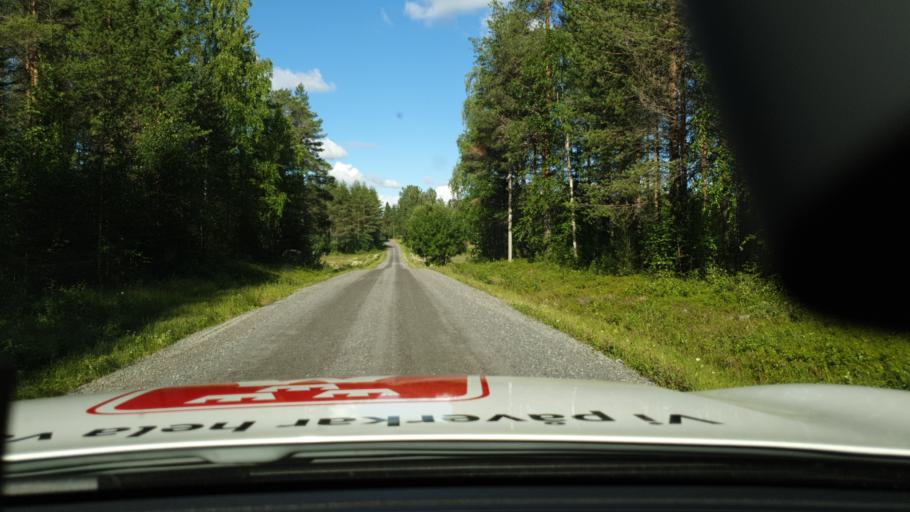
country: SE
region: Norrbotten
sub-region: Lulea Kommun
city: Ranea
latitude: 65.9909
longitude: 22.0135
